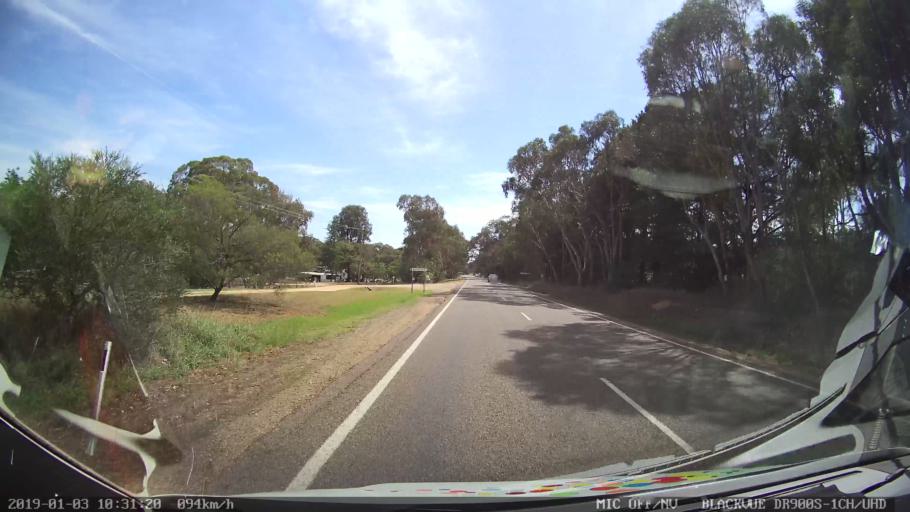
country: AU
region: New South Wales
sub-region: Young
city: Young
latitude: -34.3514
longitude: 148.2762
